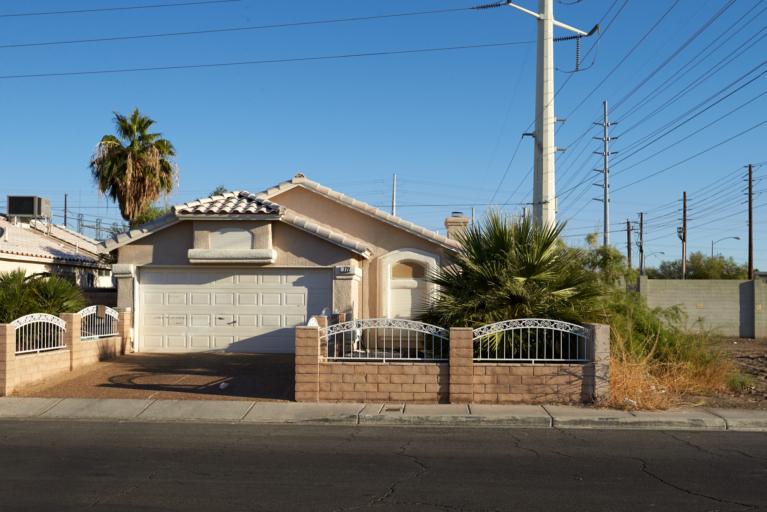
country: US
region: Nevada
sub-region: Clark County
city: Winchester
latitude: 36.1424
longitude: -115.0478
